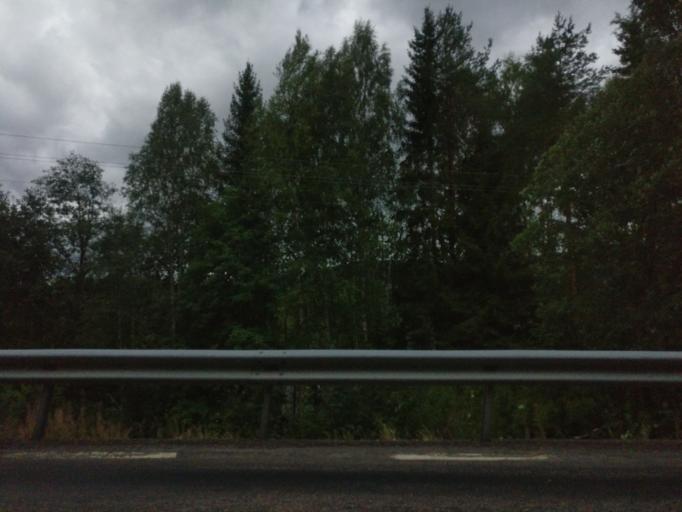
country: SE
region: Vaermland
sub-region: Torsby Kommun
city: Torsby
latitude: 60.5933
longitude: 13.0735
